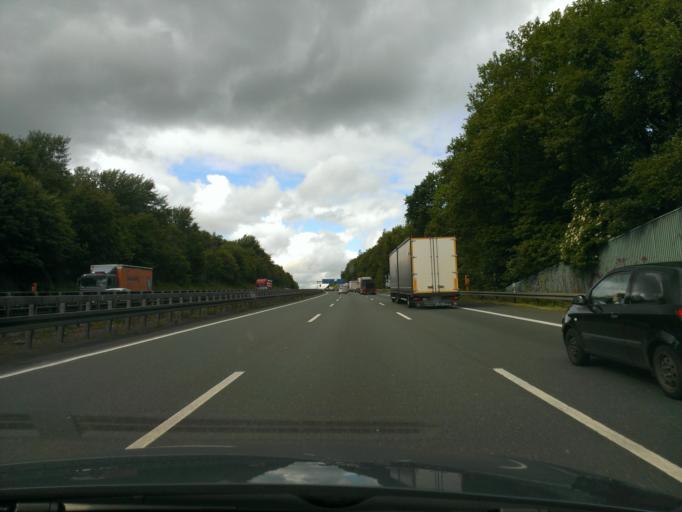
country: DE
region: North Rhine-Westphalia
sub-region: Regierungsbezirk Arnsberg
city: Schwelm
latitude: 51.3198
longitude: 7.2831
